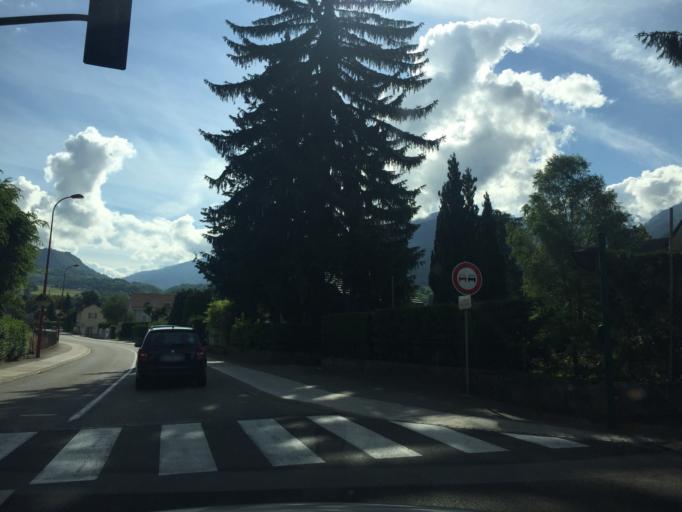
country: FR
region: Rhone-Alpes
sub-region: Departement de la Savoie
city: La Rochette
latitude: 45.4522
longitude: 6.1077
